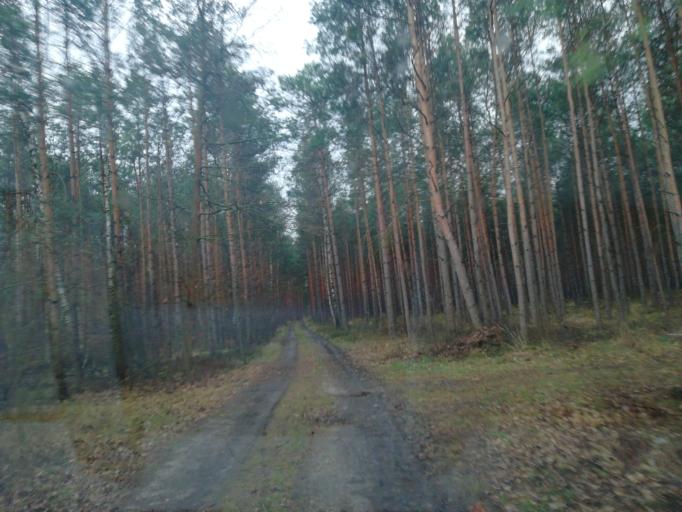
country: DE
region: Brandenburg
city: Schonborn
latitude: 51.6677
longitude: 13.4889
